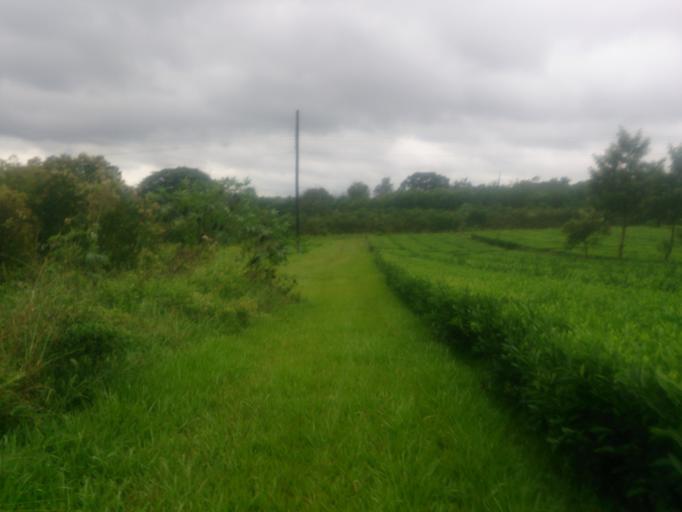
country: AR
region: Misiones
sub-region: Departamento de Obera
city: Obera
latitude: -27.4415
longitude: -55.0837
